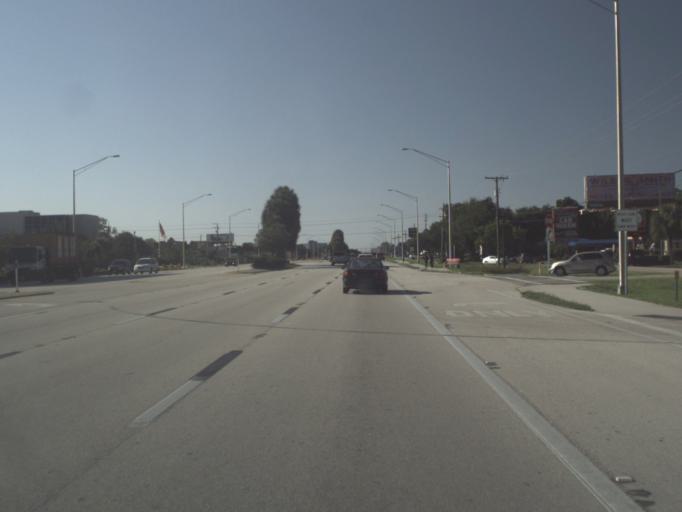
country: US
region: Florida
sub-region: Lee County
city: Pine Manor
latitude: 26.5634
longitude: -81.8720
